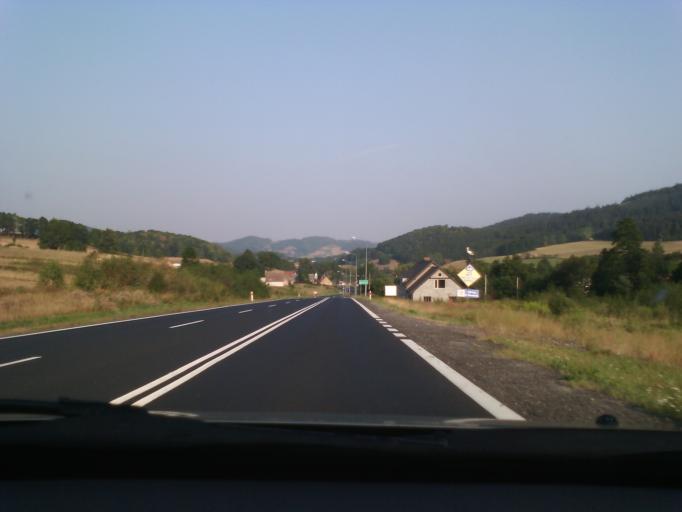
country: PL
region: Lower Silesian Voivodeship
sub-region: Powiat jeleniogorski
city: Janowice Wielkie
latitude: 50.9101
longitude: 15.9317
